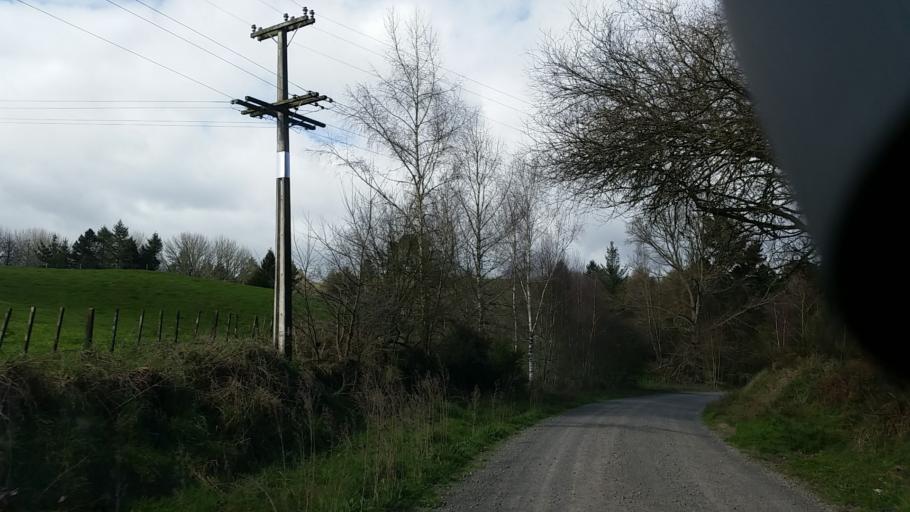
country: NZ
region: Waikato
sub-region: South Waikato District
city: Tokoroa
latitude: -38.3778
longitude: 176.0864
